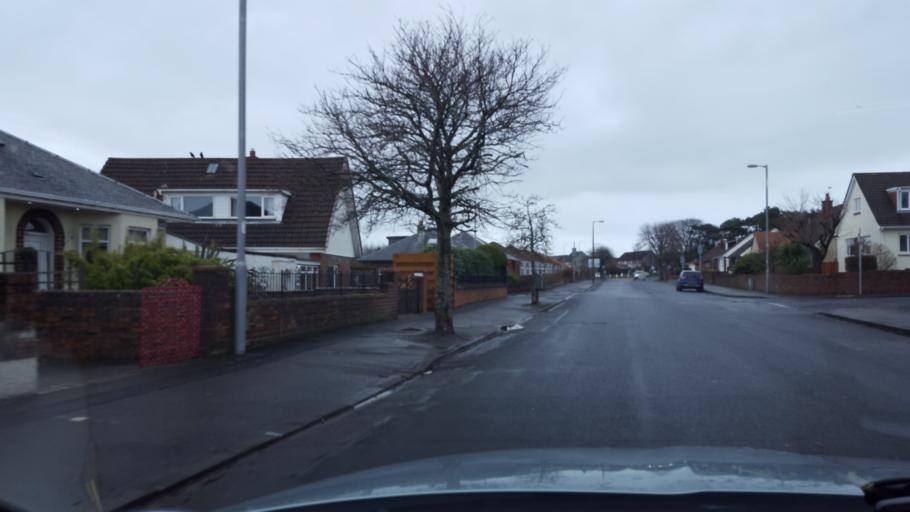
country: GB
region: Scotland
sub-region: South Ayrshire
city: Ayr
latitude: 55.4472
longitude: -4.6172
